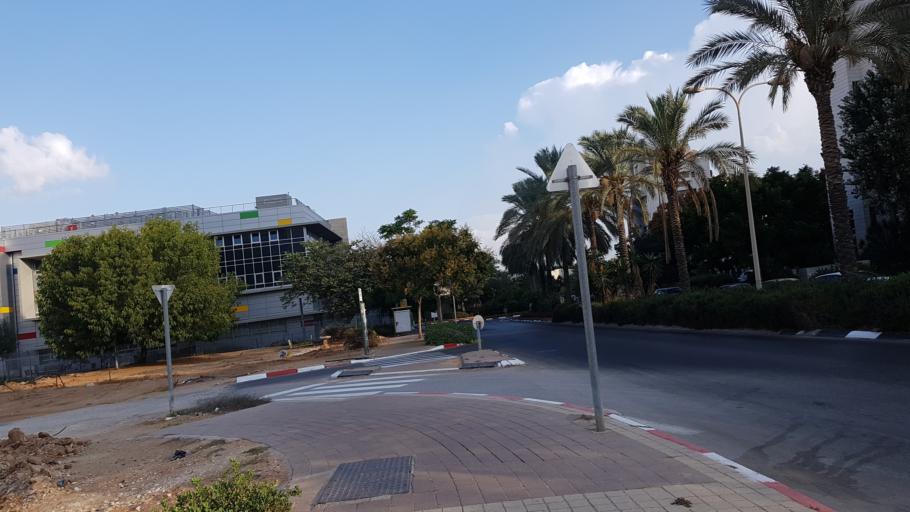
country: IL
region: Central District
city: Ness Ziona
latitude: 31.9057
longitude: 34.8207
